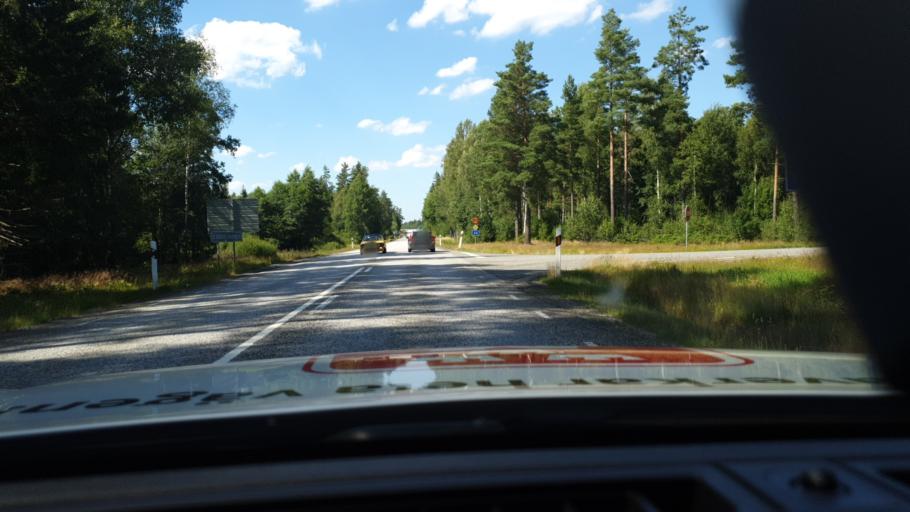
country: SE
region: Joenkoeping
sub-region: Jonkopings Kommun
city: Odensjo
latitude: 57.6080
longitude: 14.2150
